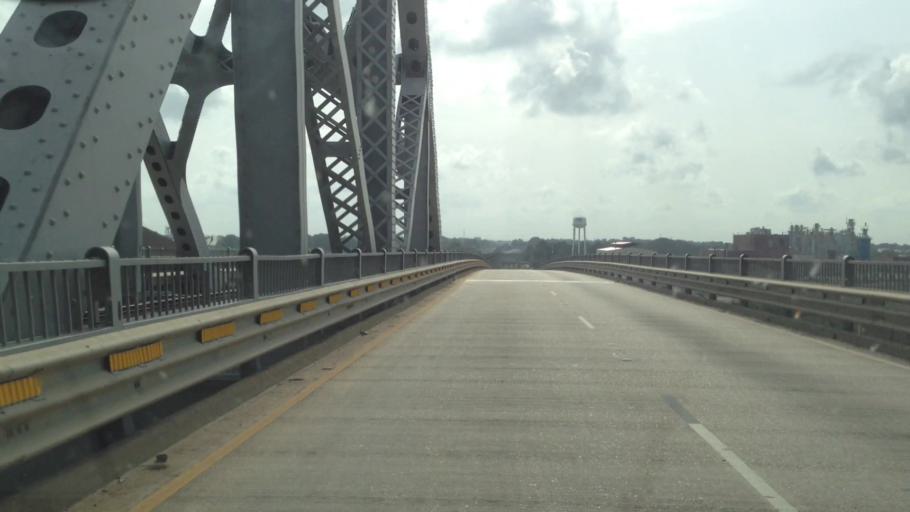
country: US
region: Louisiana
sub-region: West Baton Rouge Parish
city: Port Allen
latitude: 30.5073
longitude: -91.1939
